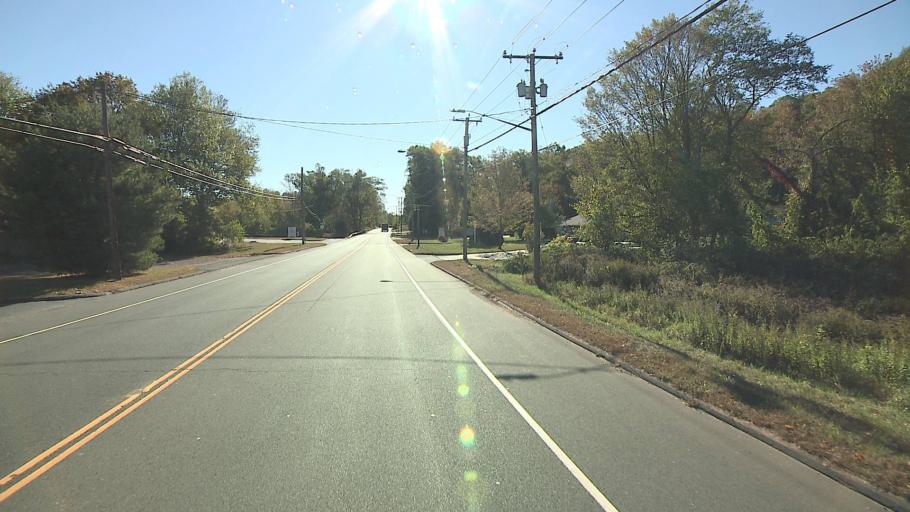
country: US
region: Connecticut
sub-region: Middlesex County
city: Portland
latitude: 41.5716
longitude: -72.5988
